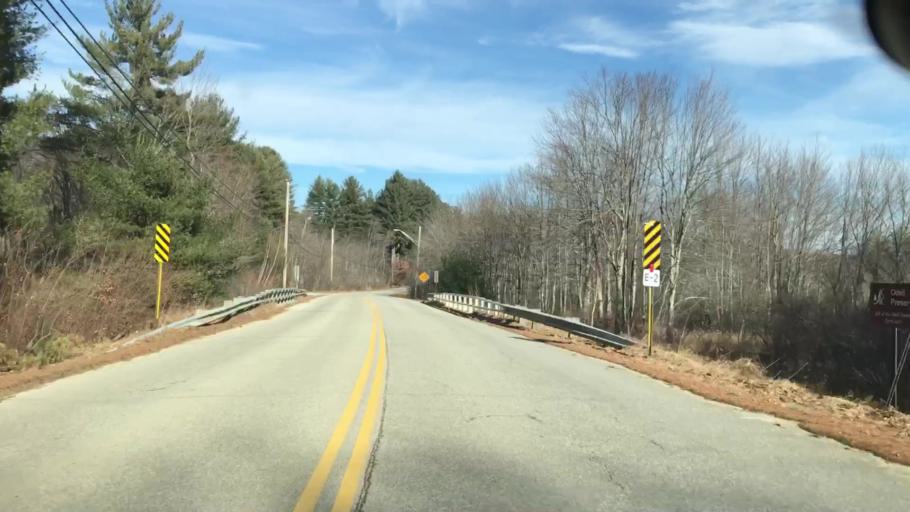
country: US
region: New Hampshire
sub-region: Hillsborough County
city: Mont Vernon
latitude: 42.9011
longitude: -71.6028
